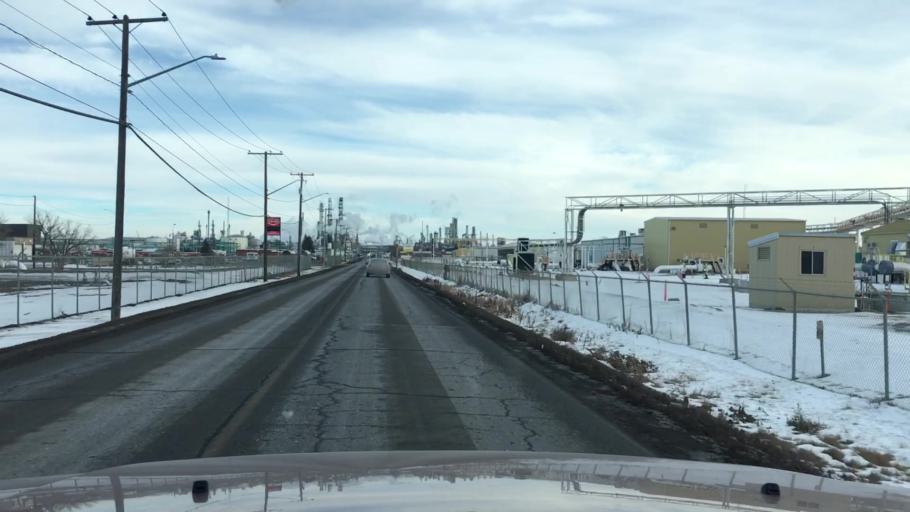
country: CA
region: Saskatchewan
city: Regina
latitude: 50.4843
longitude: -104.5897
